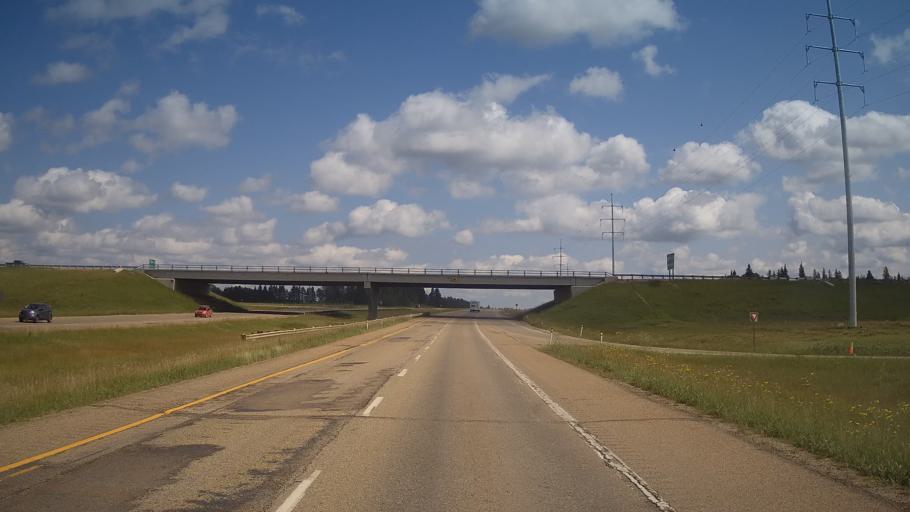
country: CA
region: Alberta
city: Sherwood Park
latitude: 53.4466
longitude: -113.2484
